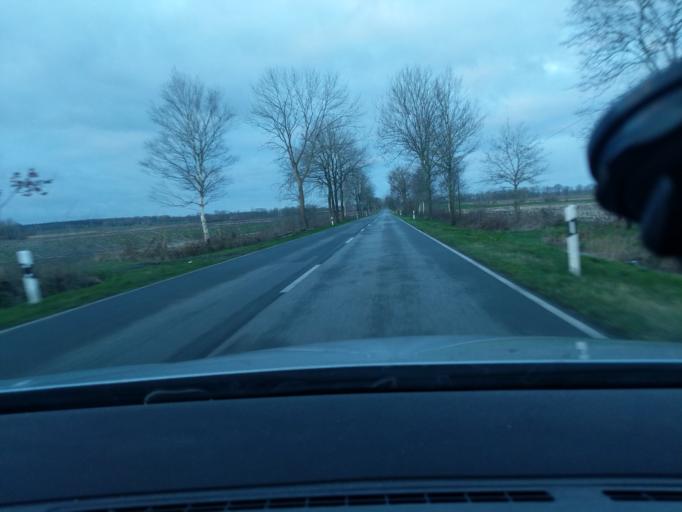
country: DE
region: Lower Saxony
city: Lintig
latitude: 53.6168
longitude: 8.9224
